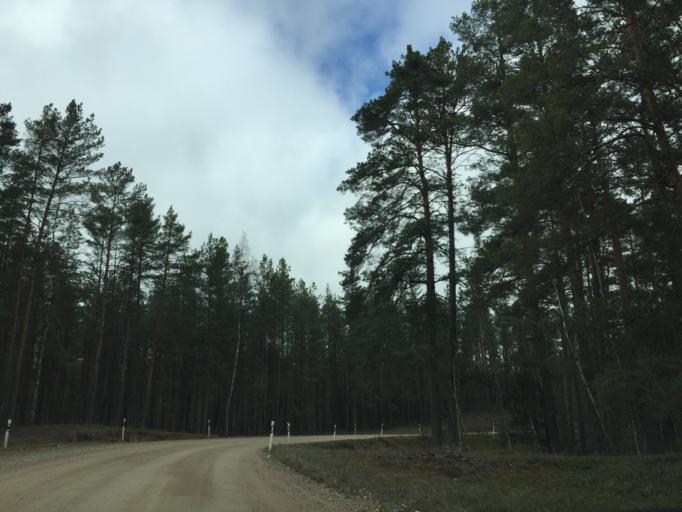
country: EE
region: Valgamaa
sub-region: Valga linn
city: Valga
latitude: 57.6617
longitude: 26.2010
